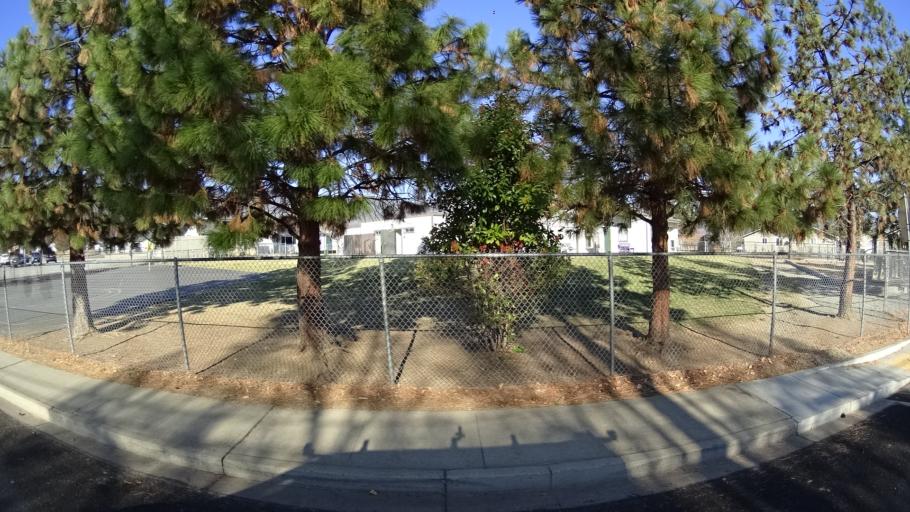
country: US
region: California
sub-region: Siskiyou County
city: Yreka
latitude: 41.7249
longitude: -122.6424
